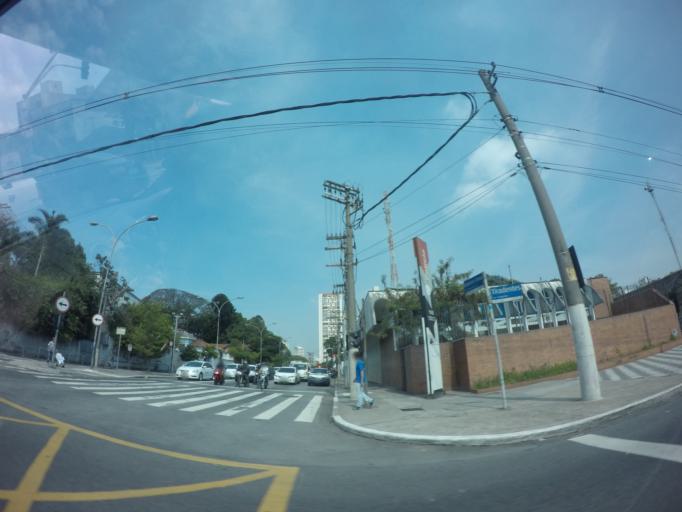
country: BR
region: Sao Paulo
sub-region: Sao Paulo
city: Sao Paulo
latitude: -23.5323
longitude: -46.6328
